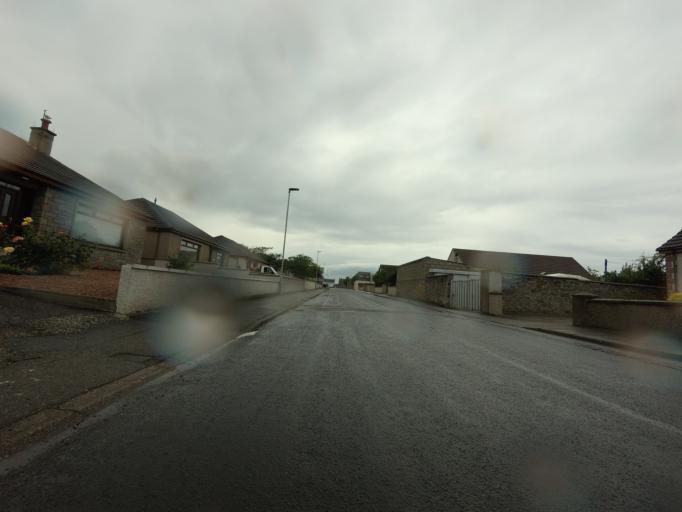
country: GB
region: Scotland
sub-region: Moray
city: Buckie
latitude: 57.6773
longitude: -2.9587
